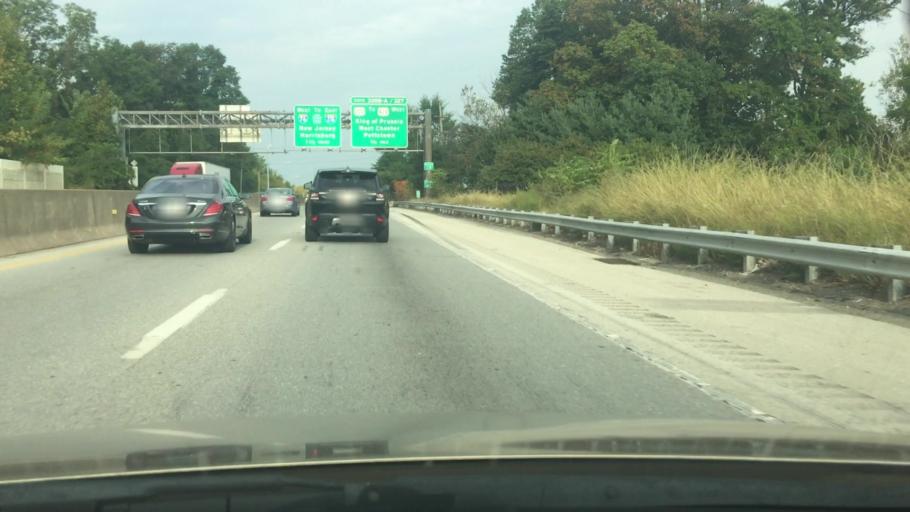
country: US
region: Pennsylvania
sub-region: Montgomery County
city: King of Prussia
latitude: 40.0787
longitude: -75.3757
